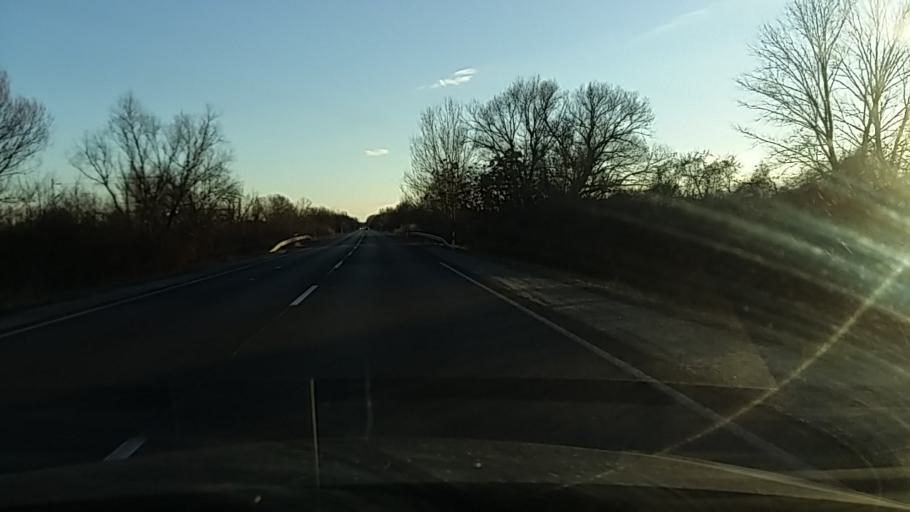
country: HU
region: Szabolcs-Szatmar-Bereg
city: Ujfeherto
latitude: 47.8535
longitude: 21.7038
